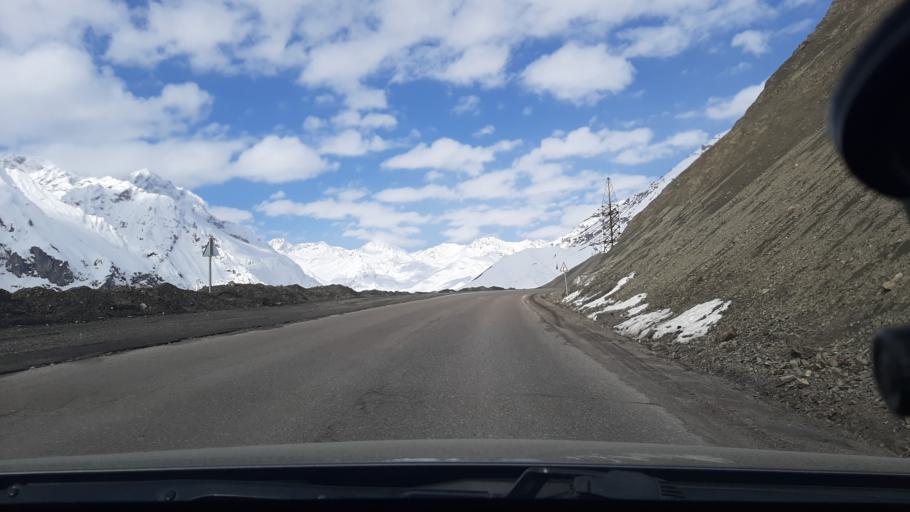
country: TJ
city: Tagob
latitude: 39.0578
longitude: 68.7205
